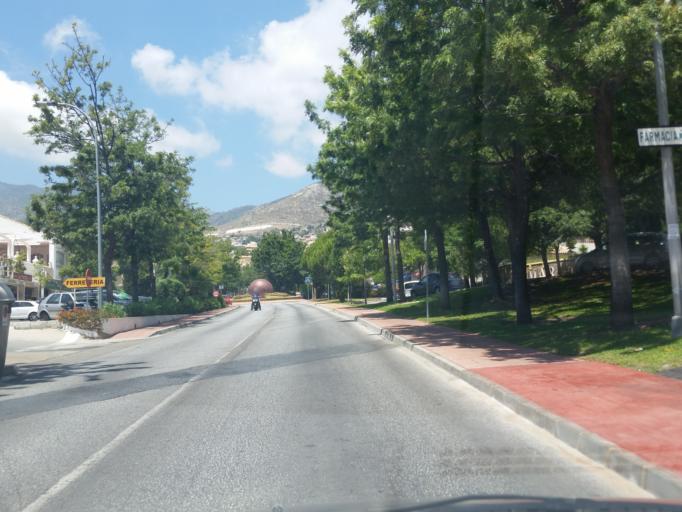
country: ES
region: Andalusia
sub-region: Provincia de Malaga
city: Benalmadena
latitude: 36.6001
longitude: -4.5431
